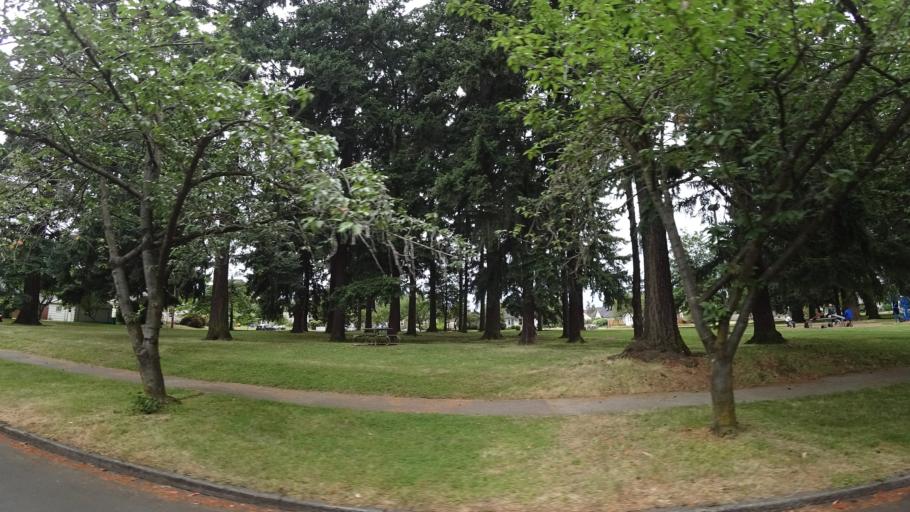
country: US
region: Oregon
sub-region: Multnomah County
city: Portland
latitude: 45.5751
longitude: -122.6935
